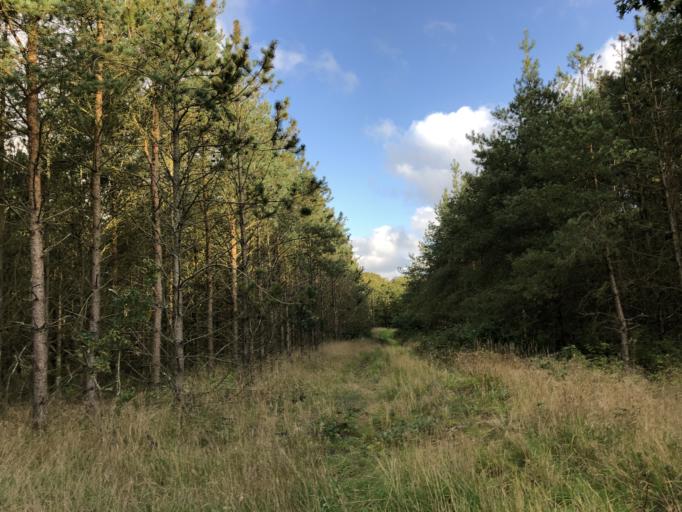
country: DK
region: Central Jutland
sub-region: Holstebro Kommune
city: Ulfborg
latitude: 56.3743
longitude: 8.3427
